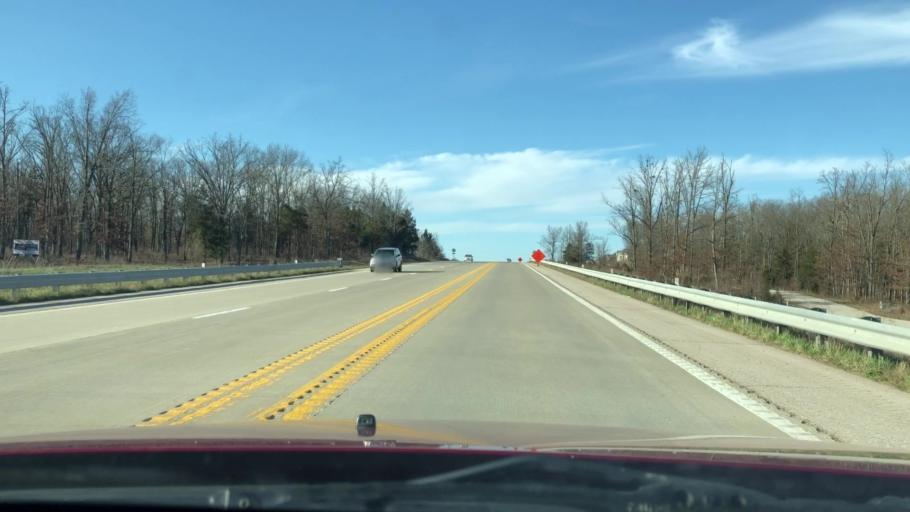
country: US
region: Missouri
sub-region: Camden County
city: Camdenton
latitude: 37.9451
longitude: -92.7157
